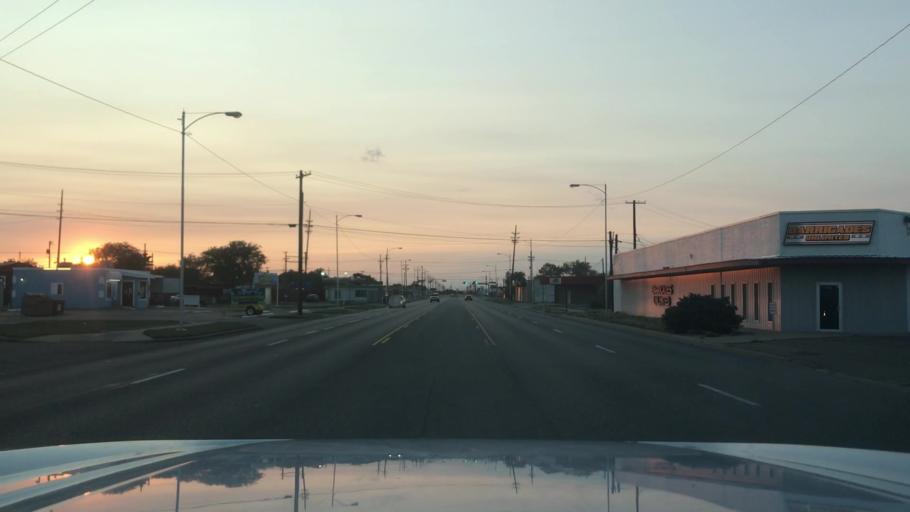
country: US
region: Texas
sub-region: Lubbock County
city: Lubbock
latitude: 33.5979
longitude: -101.8596
